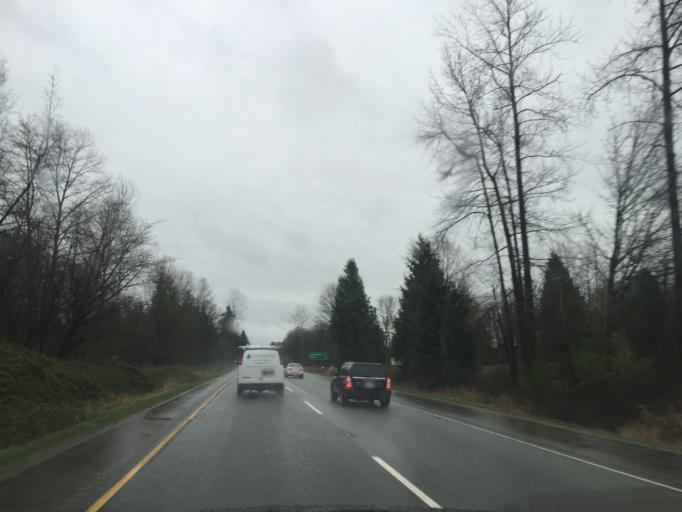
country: CA
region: British Columbia
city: Aldergrove
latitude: 49.0970
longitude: -122.4817
